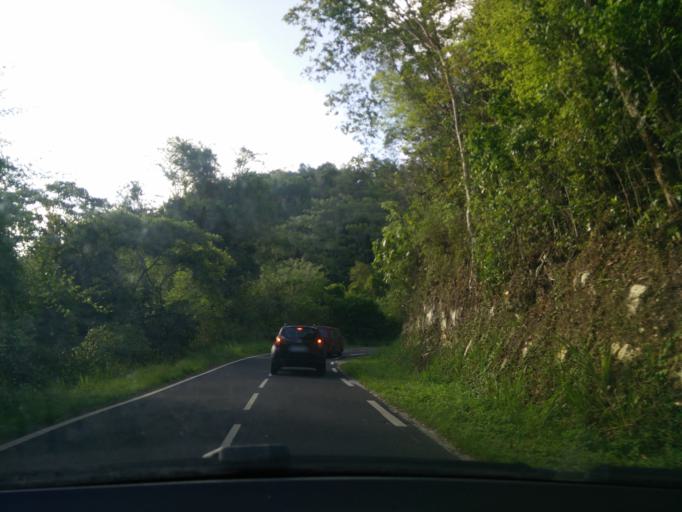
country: GP
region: Guadeloupe
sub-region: Guadeloupe
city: Sainte-Anne
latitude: 16.2662
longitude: -61.4207
